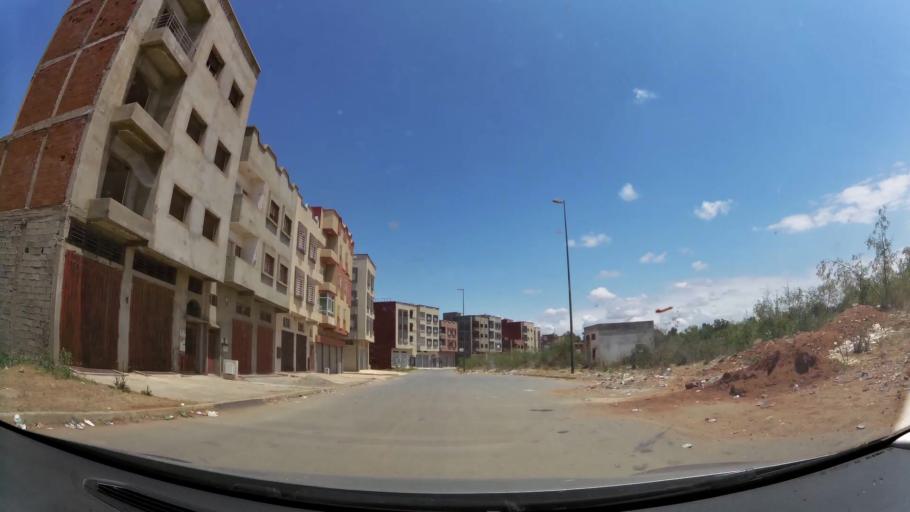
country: MA
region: Gharb-Chrarda-Beni Hssen
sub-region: Kenitra Province
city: Kenitra
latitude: 34.2302
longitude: -6.6095
